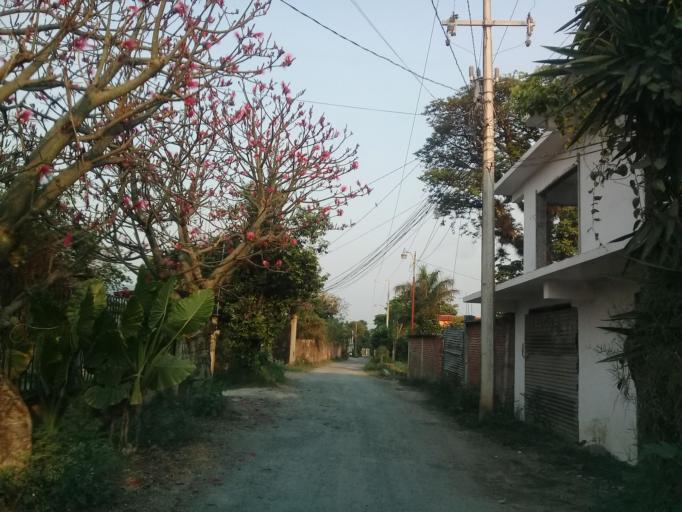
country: MX
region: Veracruz
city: Ixtac Zoquitlan
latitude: 18.8475
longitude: -97.0581
